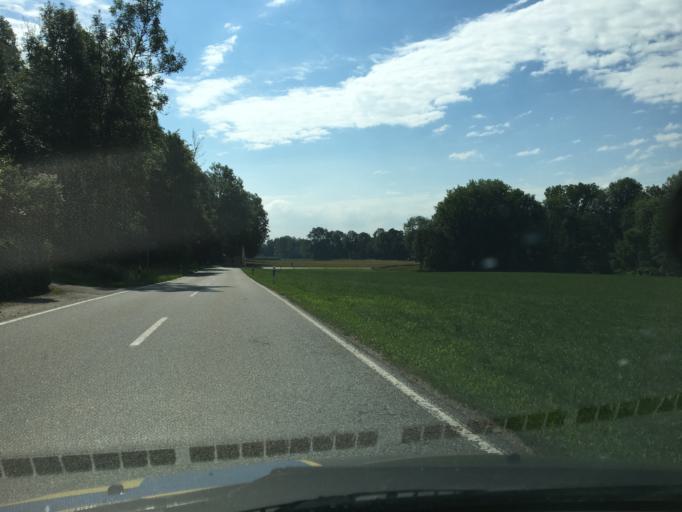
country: DE
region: Bavaria
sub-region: Upper Bavaria
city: Rohrbach
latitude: 48.2844
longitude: 12.5649
